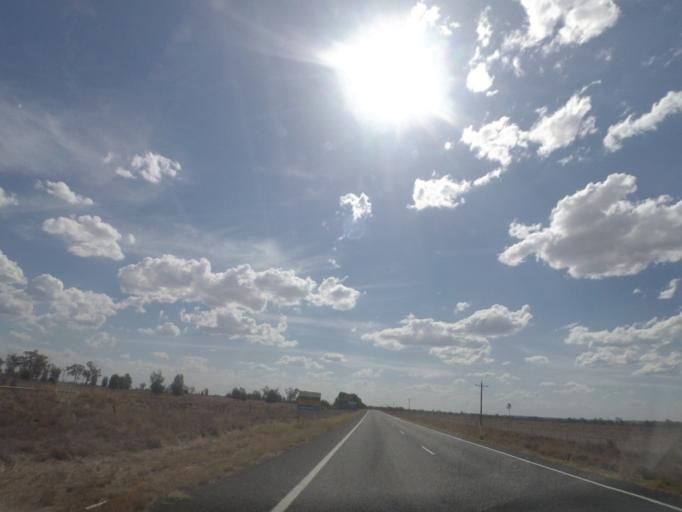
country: AU
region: New South Wales
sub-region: Moree Plains
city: Boggabilla
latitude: -28.4147
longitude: 151.1352
